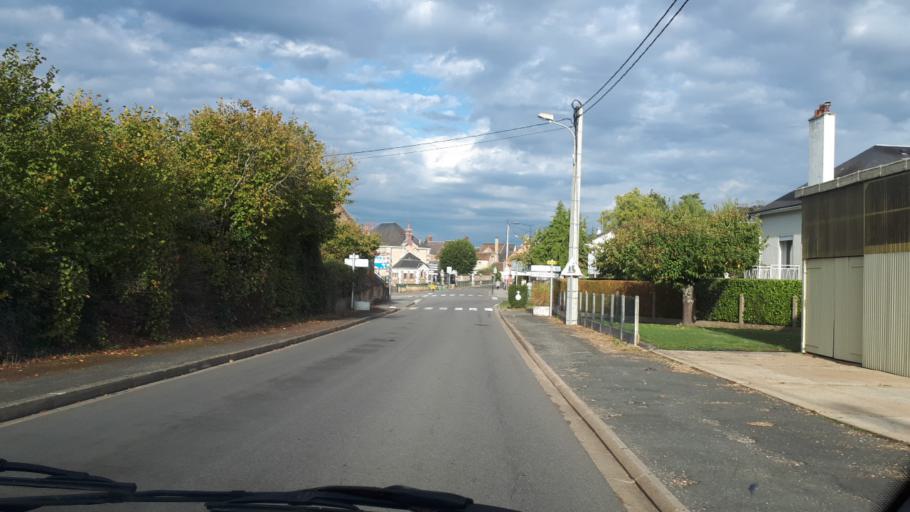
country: FR
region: Centre
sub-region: Departement du Loir-et-Cher
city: Mondoubleau
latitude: 47.9793
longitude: 0.8994
